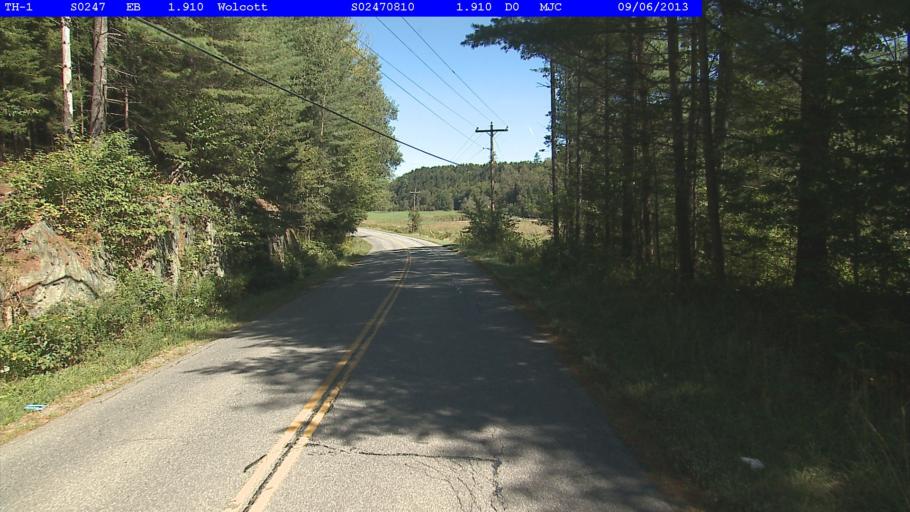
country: US
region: Vermont
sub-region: Lamoille County
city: Morrisville
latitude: 44.5832
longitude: -72.4749
